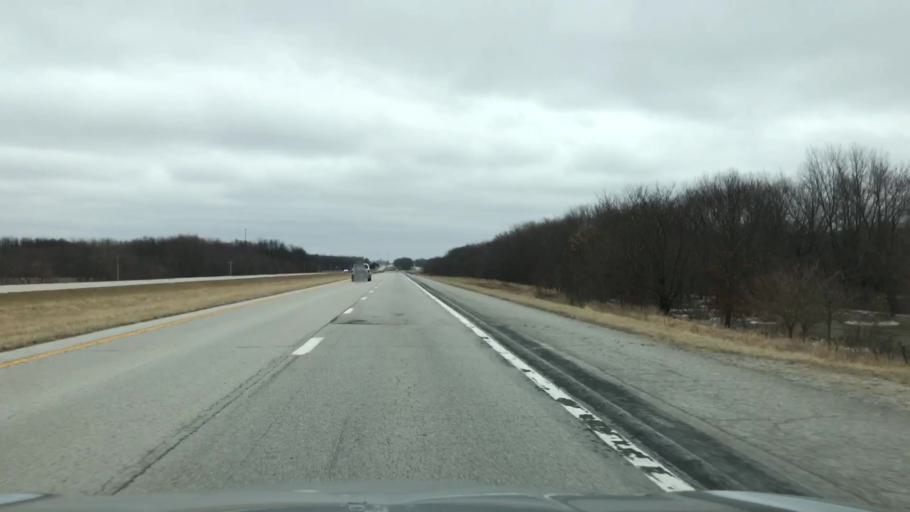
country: US
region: Missouri
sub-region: Linn County
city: Linneus
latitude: 39.7776
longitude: -93.3297
